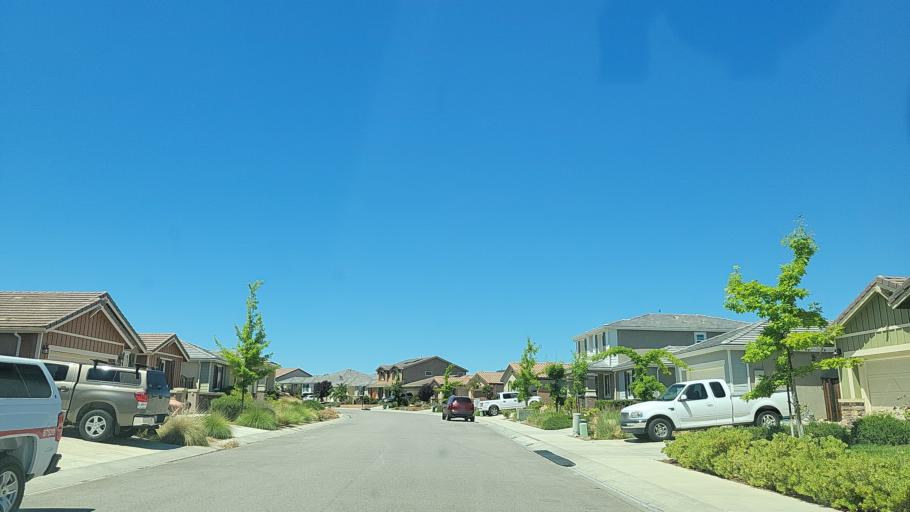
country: US
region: California
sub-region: San Luis Obispo County
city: Atascadero
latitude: 35.4512
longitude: -120.6279
